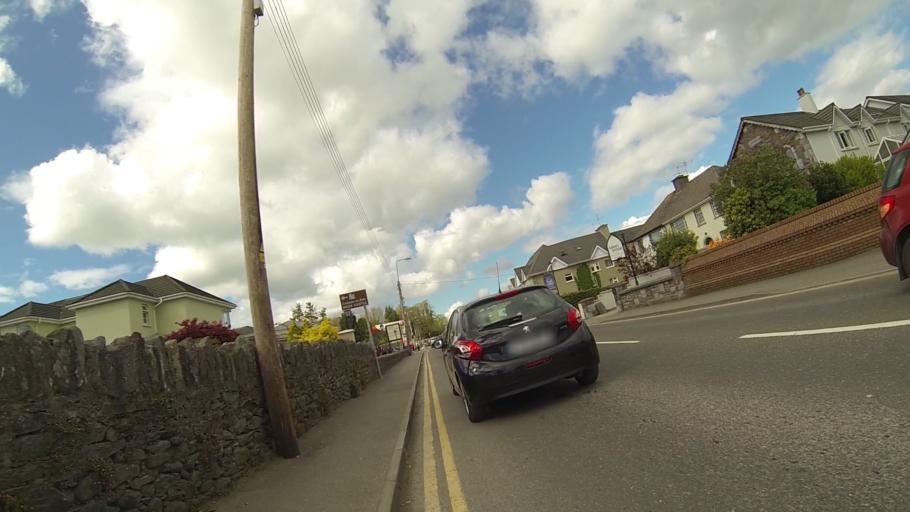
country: IE
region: Munster
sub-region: Ciarrai
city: Cill Airne
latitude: 52.0551
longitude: -9.5071
